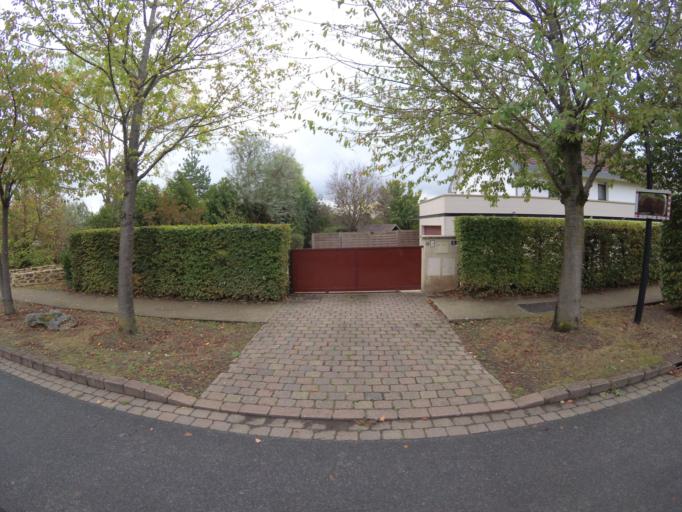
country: FR
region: Ile-de-France
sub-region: Departement de Seine-et-Marne
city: Montevrain
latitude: 48.8758
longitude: 2.7575
